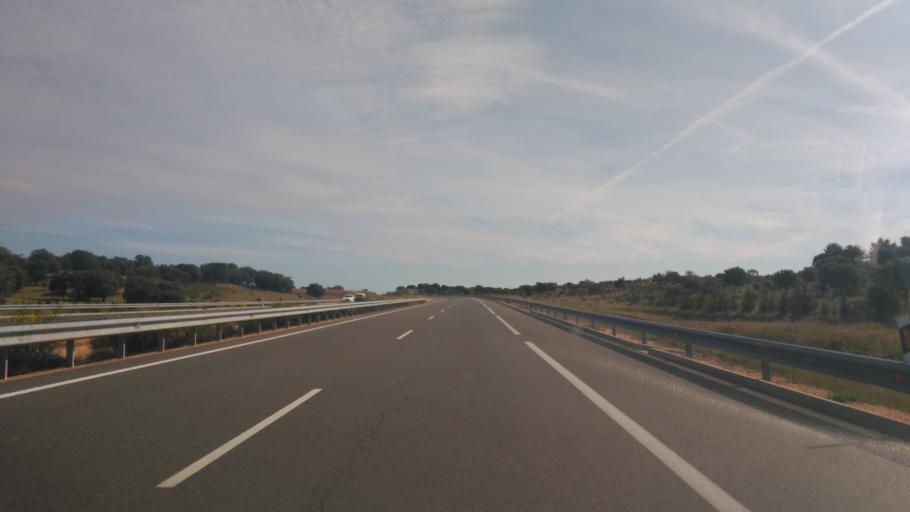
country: ES
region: Castille and Leon
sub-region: Provincia de Zamora
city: Cuelgamures
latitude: 41.2794
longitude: -5.7033
